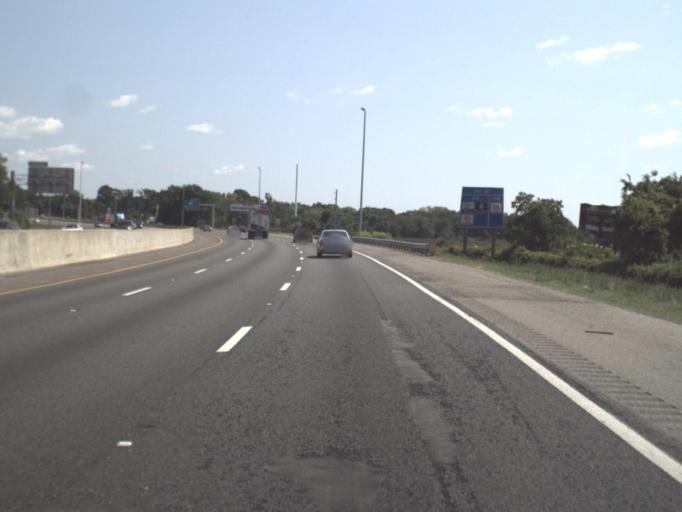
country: US
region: Florida
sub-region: Duval County
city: Jacksonville
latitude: 30.3857
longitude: -81.6695
